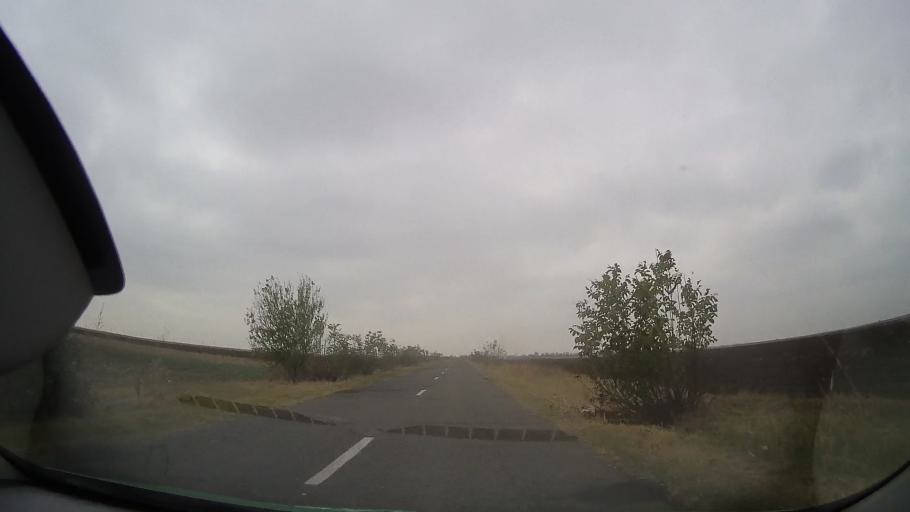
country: RO
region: Ialomita
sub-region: Comuna Valea Macrisului
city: Valea Macrisului
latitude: 44.7595
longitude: 26.8019
